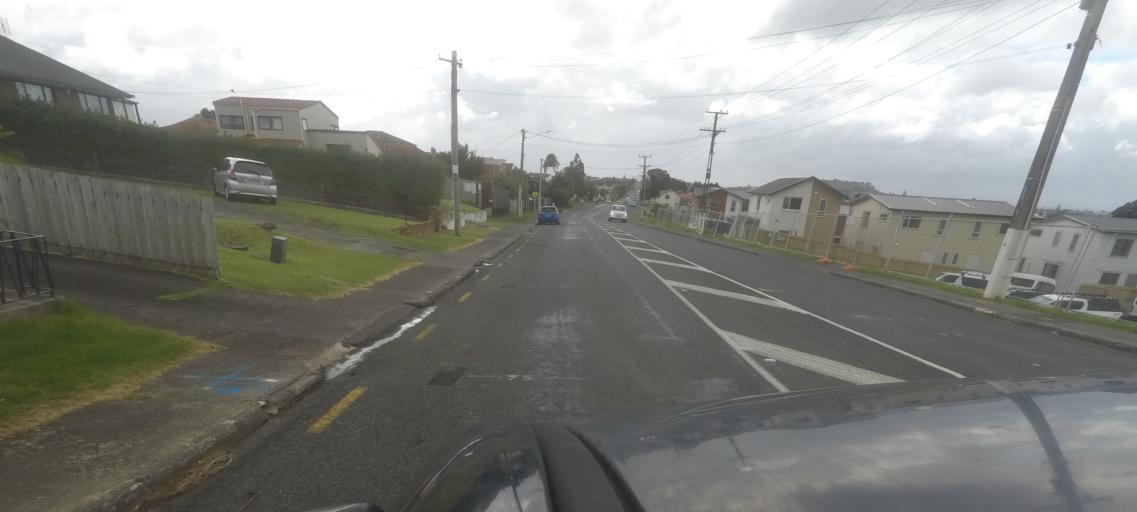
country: NZ
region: Auckland
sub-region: Auckland
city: Auckland
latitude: -36.9176
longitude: 174.7327
